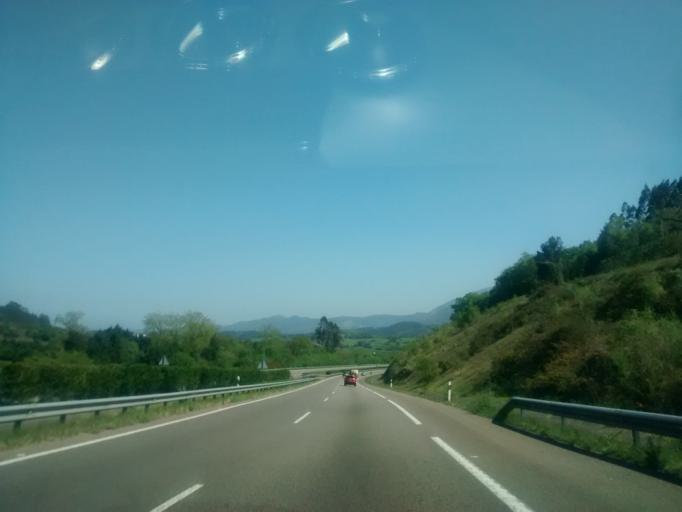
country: ES
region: Asturias
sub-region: Province of Asturias
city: Colunga
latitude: 43.4879
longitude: -5.3159
